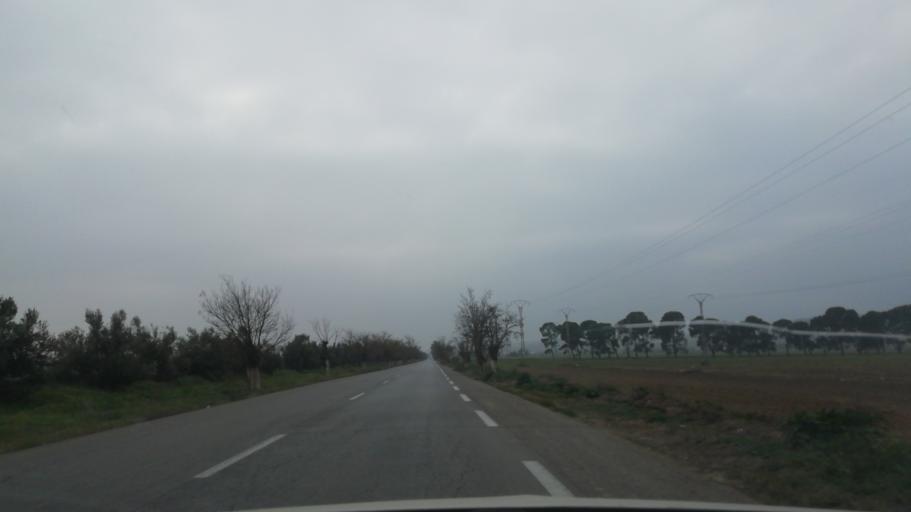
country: DZ
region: Sidi Bel Abbes
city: Sfizef
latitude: 35.2234
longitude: -0.2834
